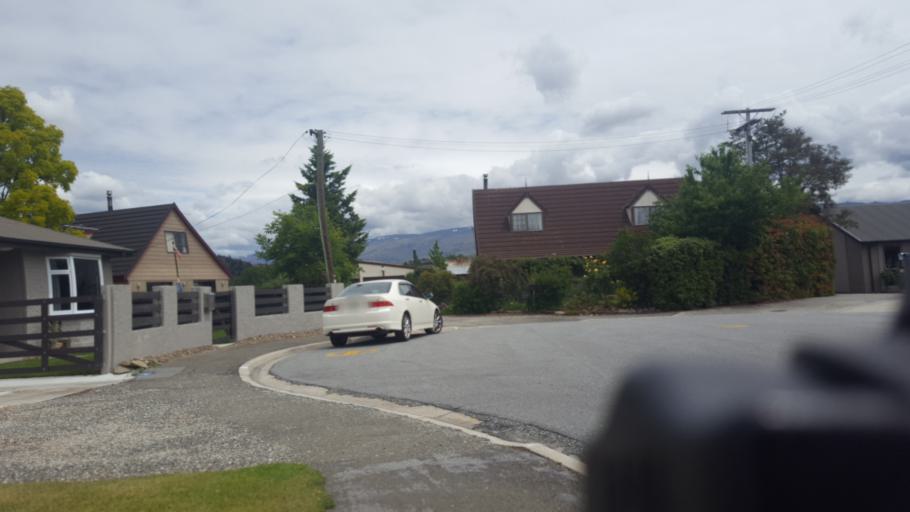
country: NZ
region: Otago
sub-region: Queenstown-Lakes District
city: Wanaka
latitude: -45.2500
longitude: 169.3789
